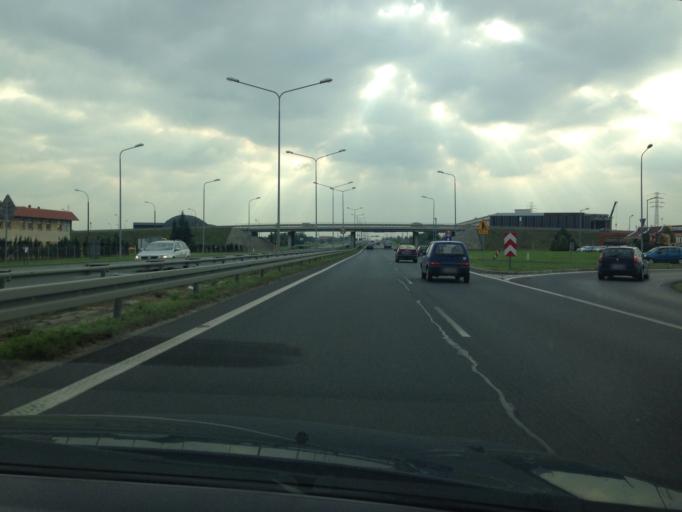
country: PL
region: Greater Poland Voivodeship
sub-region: Powiat poznanski
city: Plewiska
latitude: 52.3544
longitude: 16.8448
